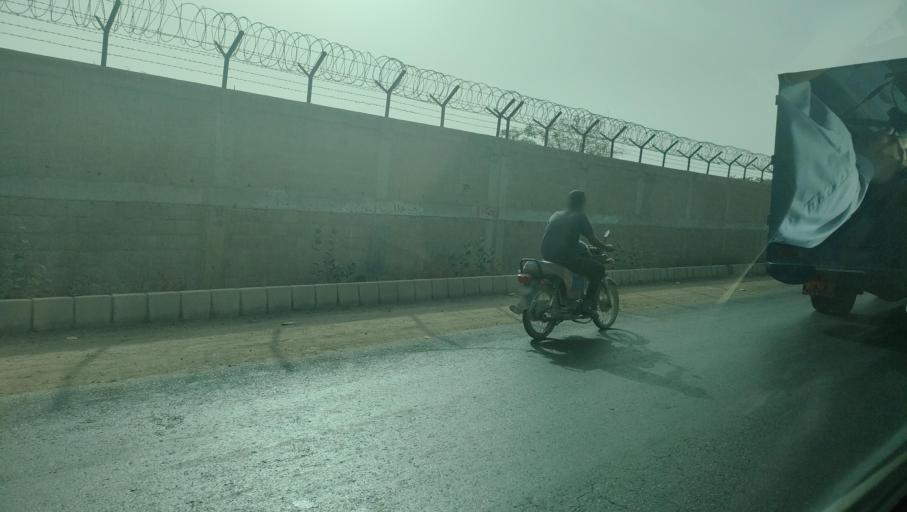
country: PK
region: Sindh
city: Malir Cantonment
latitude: 24.9182
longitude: 67.1870
